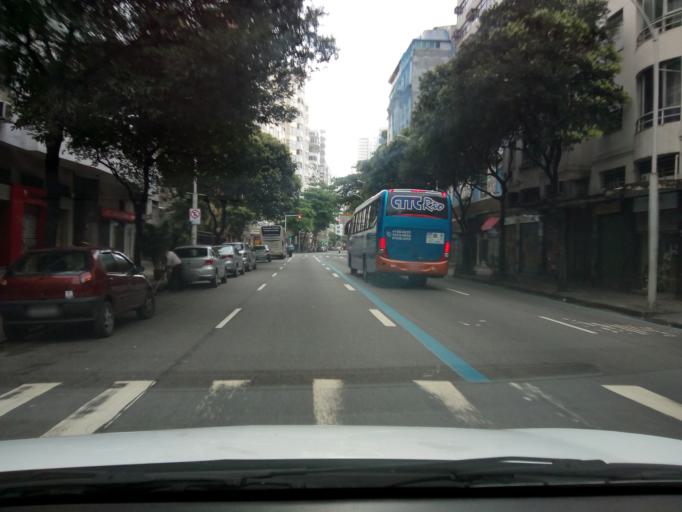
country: BR
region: Rio de Janeiro
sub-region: Rio De Janeiro
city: Rio de Janeiro
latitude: -22.9656
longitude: -43.1778
